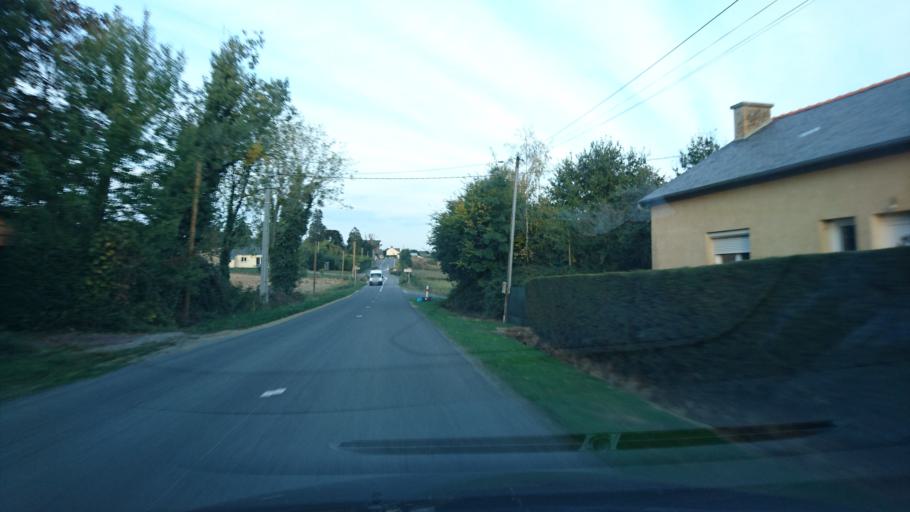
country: FR
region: Brittany
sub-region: Departement d'Ille-et-Vilaine
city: Maure-de-Bretagne
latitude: 47.8503
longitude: -2.0110
